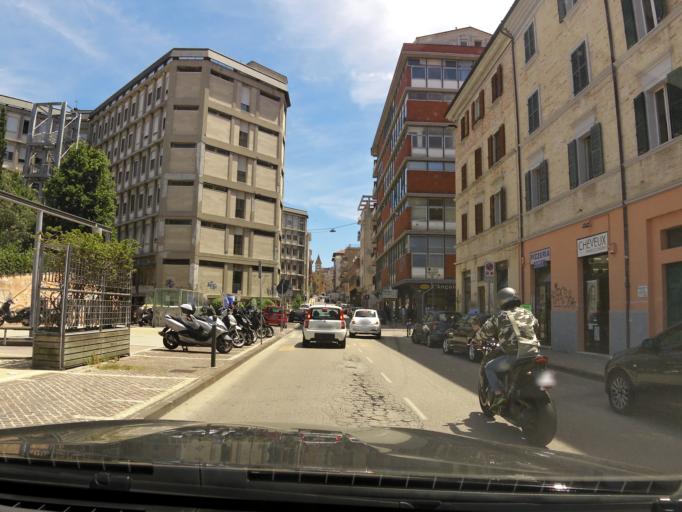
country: IT
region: The Marches
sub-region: Provincia di Ancona
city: Le Grazie di Ancona
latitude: 43.6158
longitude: 13.5150
